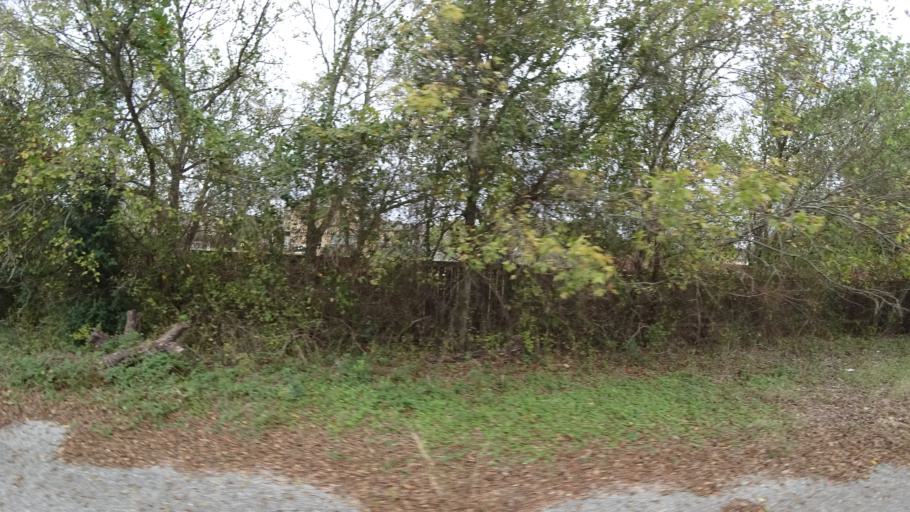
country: US
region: Texas
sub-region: Travis County
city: Shady Hollow
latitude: 30.1472
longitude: -97.8587
